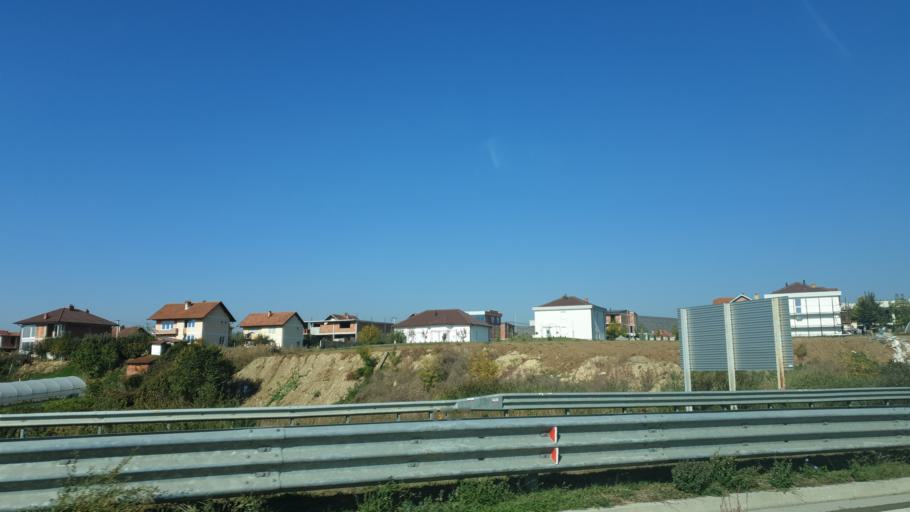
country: XK
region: Prizren
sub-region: Komuna e Therandes
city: Suva Reka
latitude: 42.3564
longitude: 20.8058
